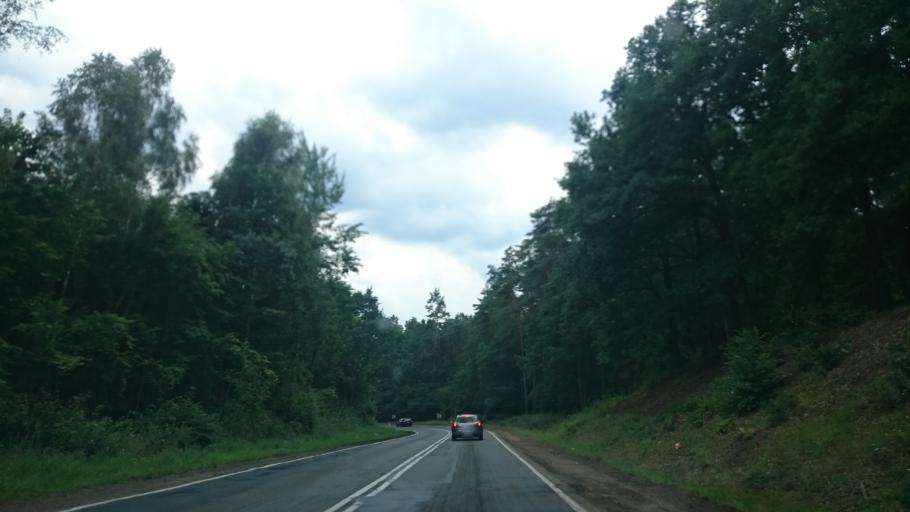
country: PL
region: Kujawsko-Pomorskie
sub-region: Powiat tucholski
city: Tuchola
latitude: 53.5565
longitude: 17.9013
